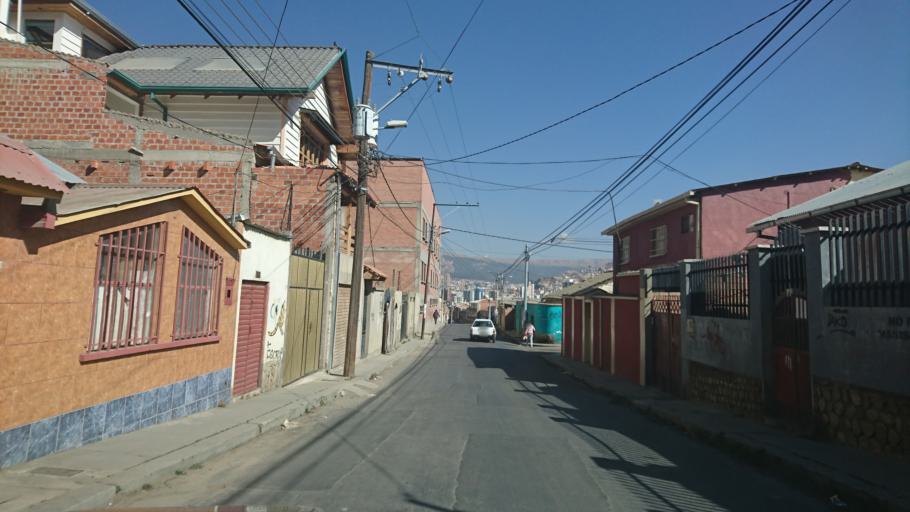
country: BO
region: La Paz
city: La Paz
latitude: -16.5089
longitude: -68.1091
